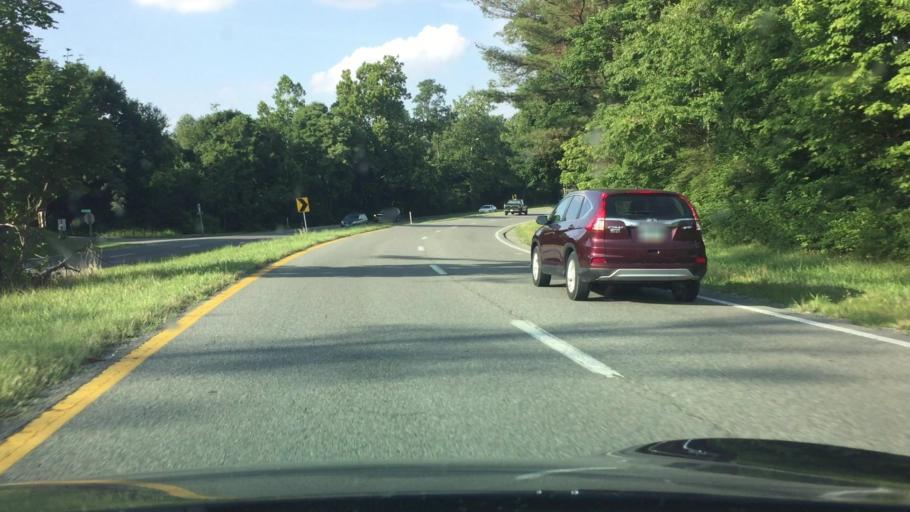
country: US
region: Virginia
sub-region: Pulaski County
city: Fairlawn
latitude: 37.1448
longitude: -80.6029
